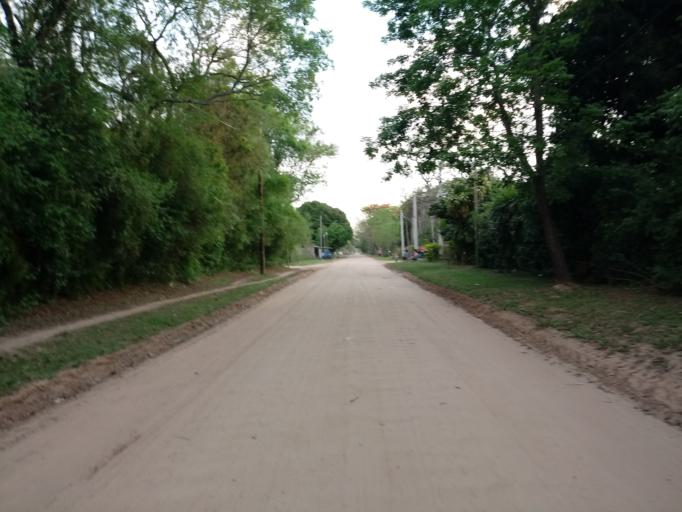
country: AR
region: Corrientes
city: San Luis del Palmar
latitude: -27.4519
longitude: -58.6547
